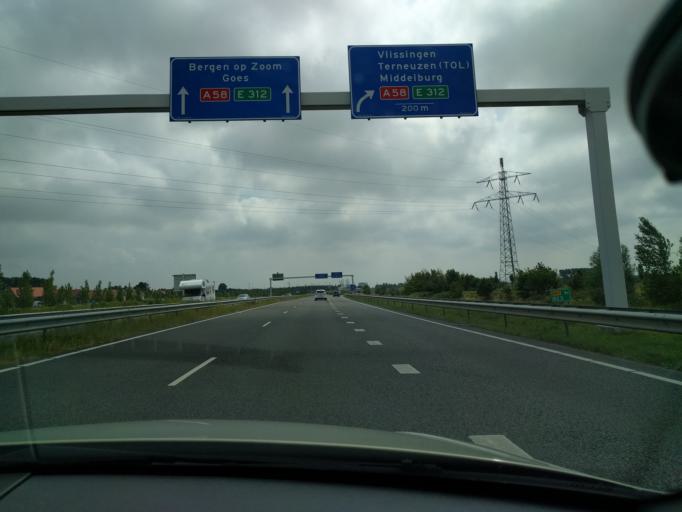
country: NL
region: Zeeland
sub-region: Gemeente Middelburg
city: Middelburg
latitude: 51.4865
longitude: 3.6468
